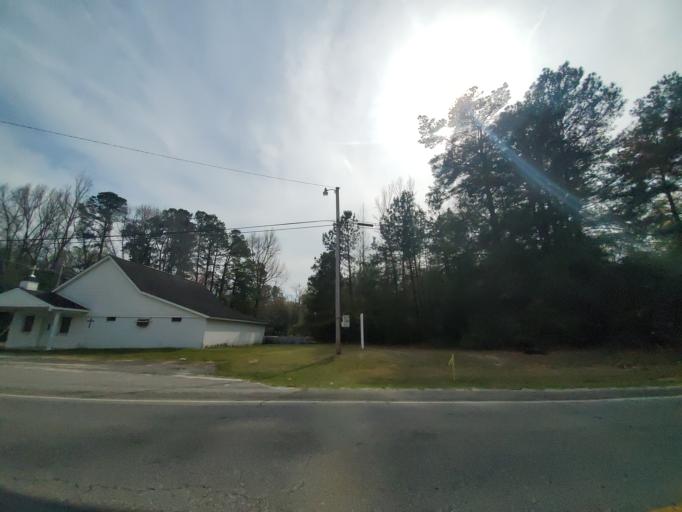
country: US
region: South Carolina
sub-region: Bamberg County
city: Bamberg
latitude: 33.3006
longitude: -81.0483
